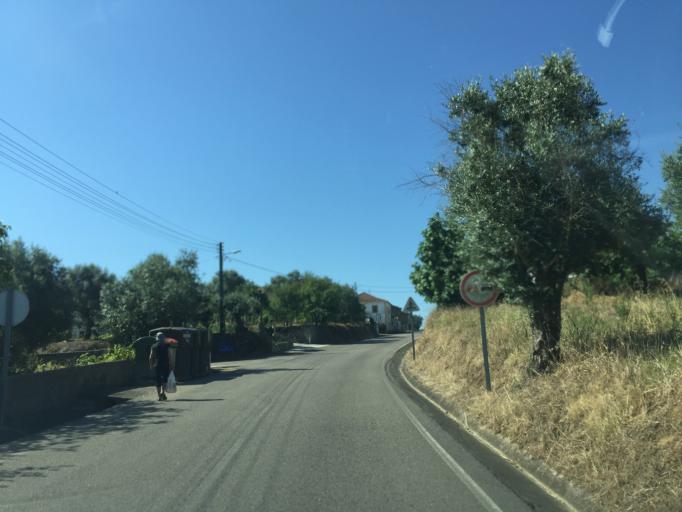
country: PT
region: Santarem
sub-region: Tomar
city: Tomar
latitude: 39.5837
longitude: -8.3275
